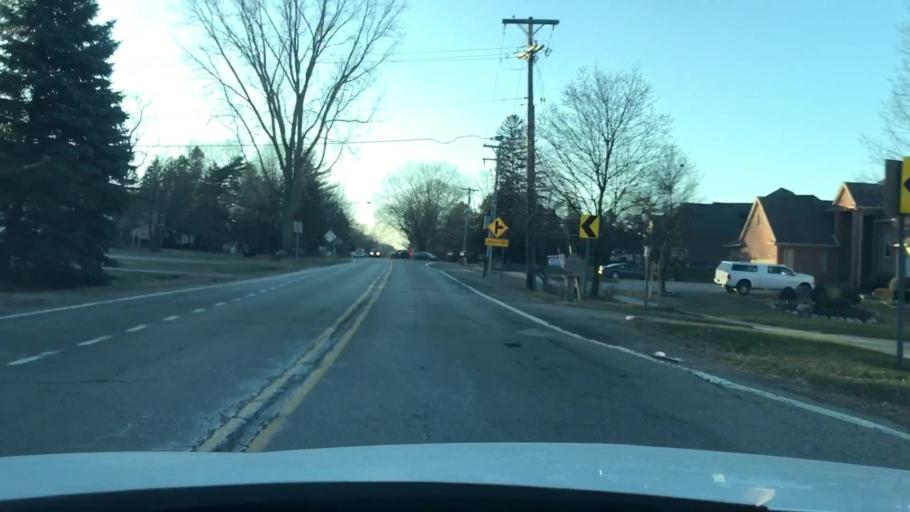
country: US
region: Michigan
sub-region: Oakland County
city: West Bloomfield Township
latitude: 42.5998
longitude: -83.4110
